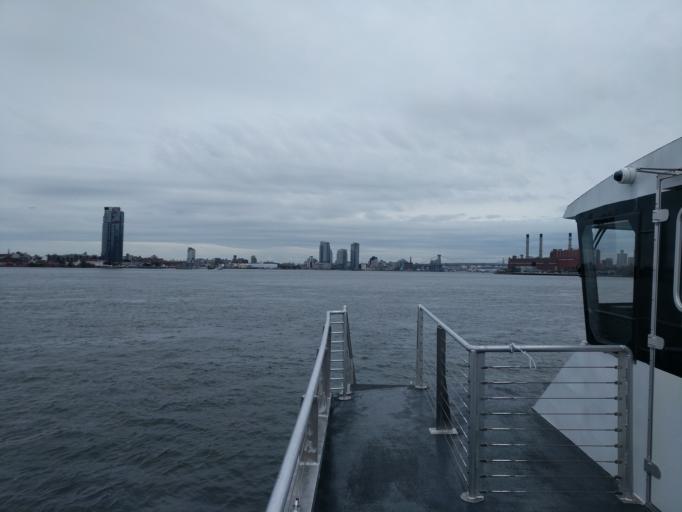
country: US
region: New York
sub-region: Queens County
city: Long Island City
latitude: 40.7412
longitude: -73.9699
